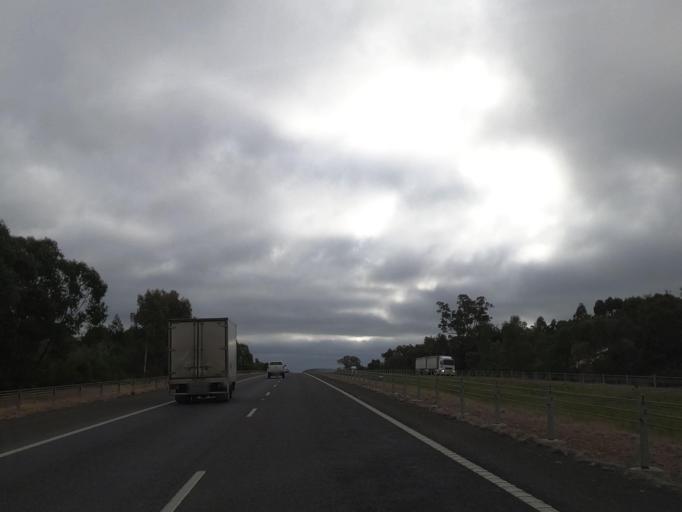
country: AU
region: Victoria
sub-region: Mount Alexander
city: Castlemaine
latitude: -37.0599
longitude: 144.3034
